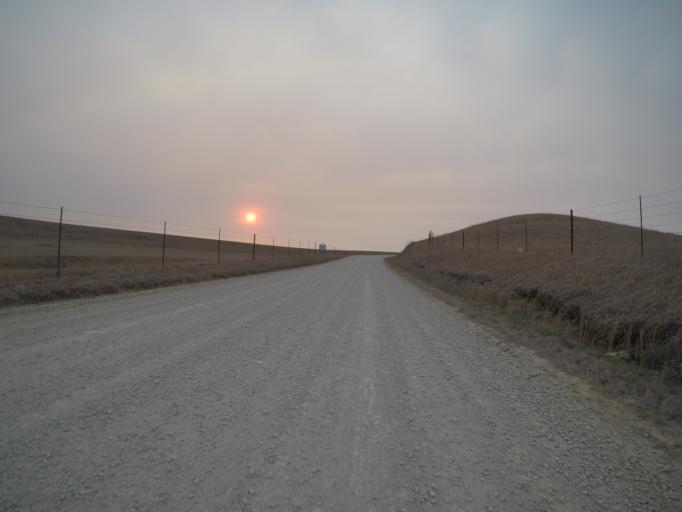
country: US
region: Kansas
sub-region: Riley County
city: Manhattan
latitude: 39.2284
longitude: -96.6398
